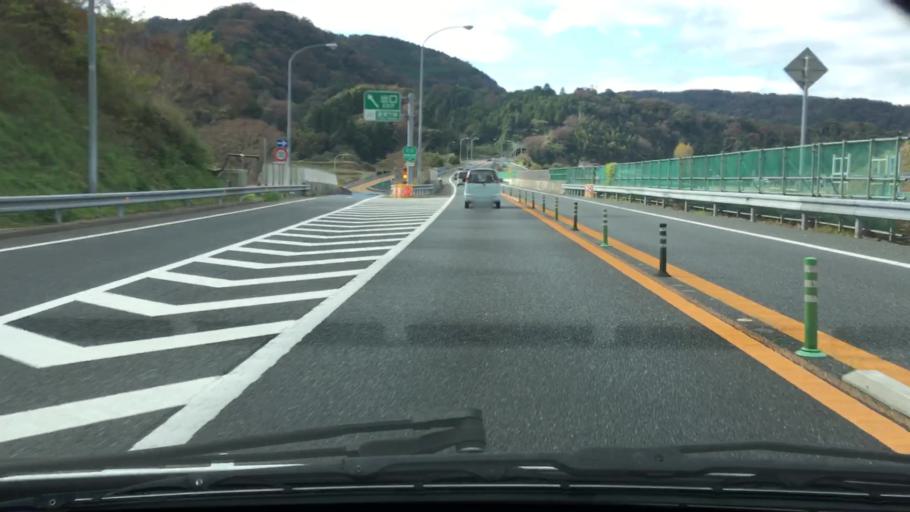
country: JP
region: Chiba
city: Futtsu
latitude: 35.1972
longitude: 139.8614
